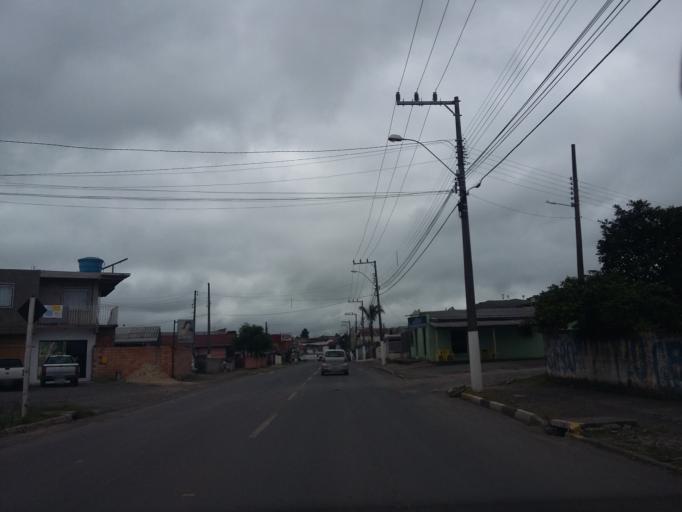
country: BR
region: Santa Catarina
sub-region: Lages
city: Lages
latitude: -27.8112
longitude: -50.2923
